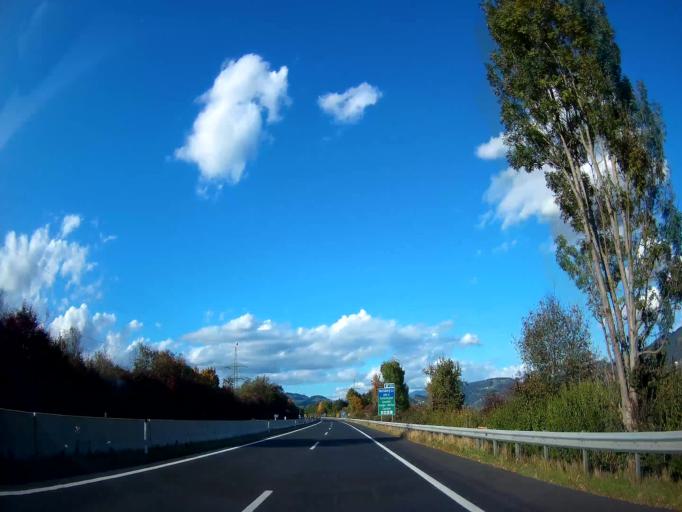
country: AT
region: Carinthia
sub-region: Politischer Bezirk Wolfsberg
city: Wolfsberg
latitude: 46.8144
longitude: 14.8229
